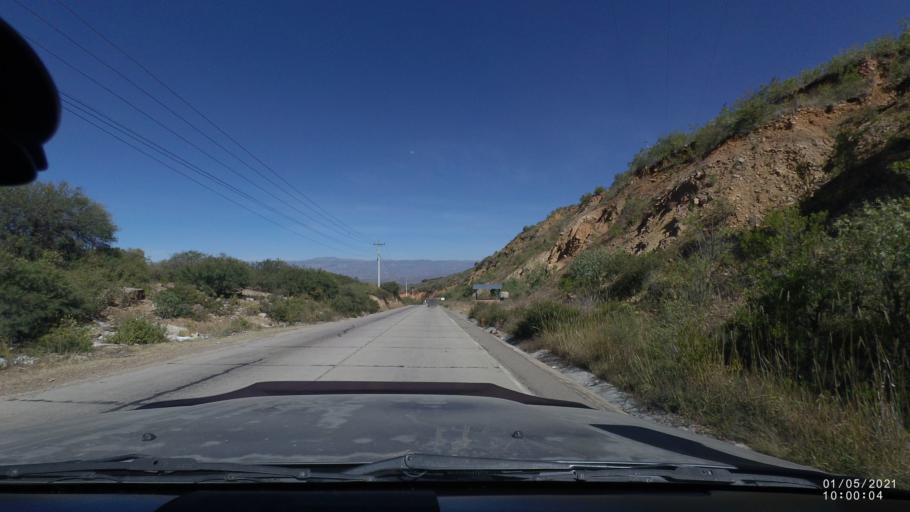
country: BO
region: Cochabamba
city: Cochabamba
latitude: -17.5293
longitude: -66.1939
